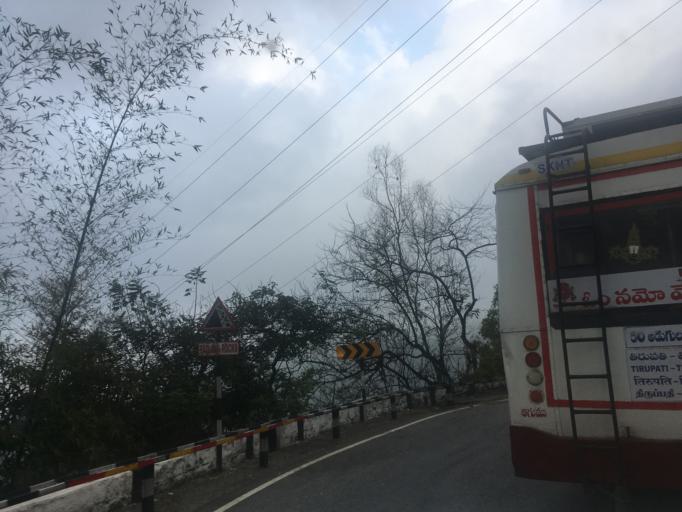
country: IN
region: Andhra Pradesh
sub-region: Chittoor
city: Tirumala
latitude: 13.6692
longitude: 79.3483
